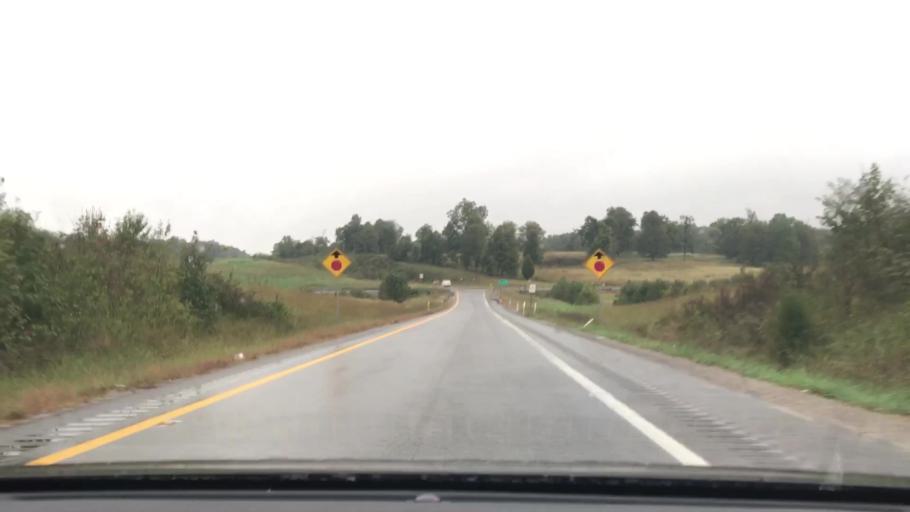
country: US
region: Kentucky
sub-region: Webster County
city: Sebree
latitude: 37.4879
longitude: -87.4748
